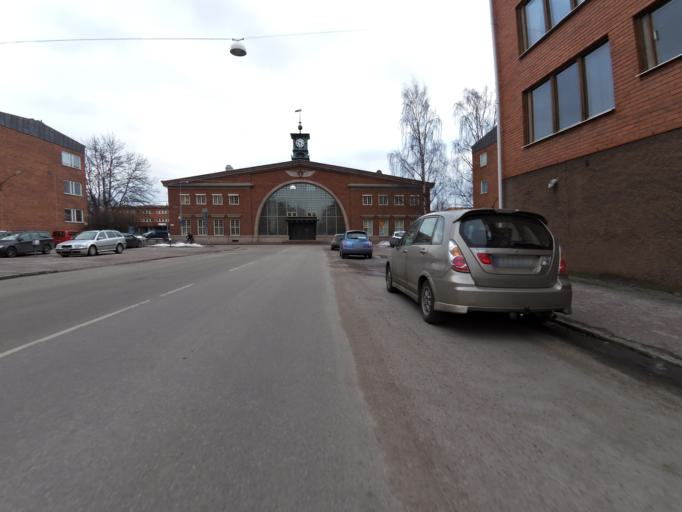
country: SE
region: Gaevleborg
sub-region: Gavle Kommun
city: Gavle
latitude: 60.6717
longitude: 17.1541
